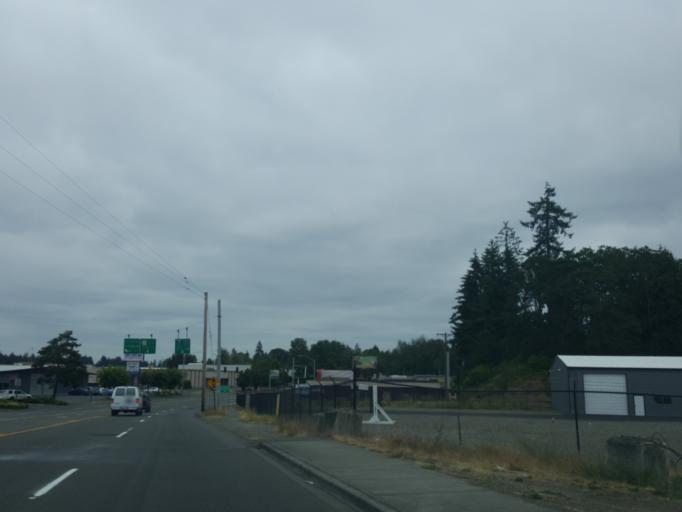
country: US
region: Washington
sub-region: Pierce County
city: Lakewood
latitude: 47.1667
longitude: -122.4933
